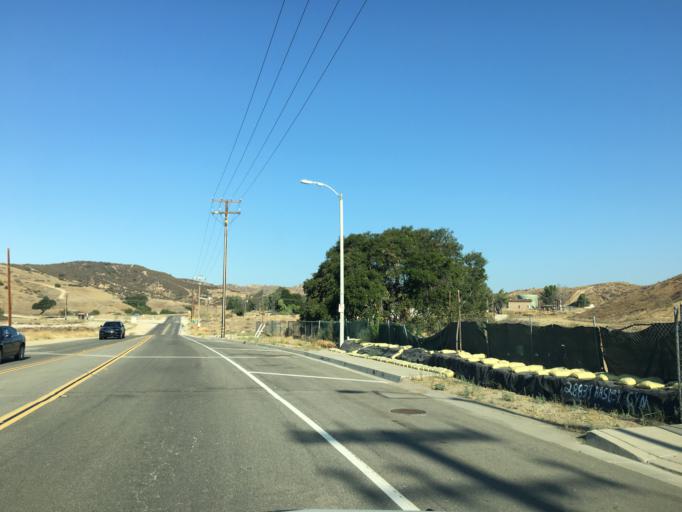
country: US
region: California
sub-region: Los Angeles County
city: Val Verde
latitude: 34.4572
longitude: -118.6385
